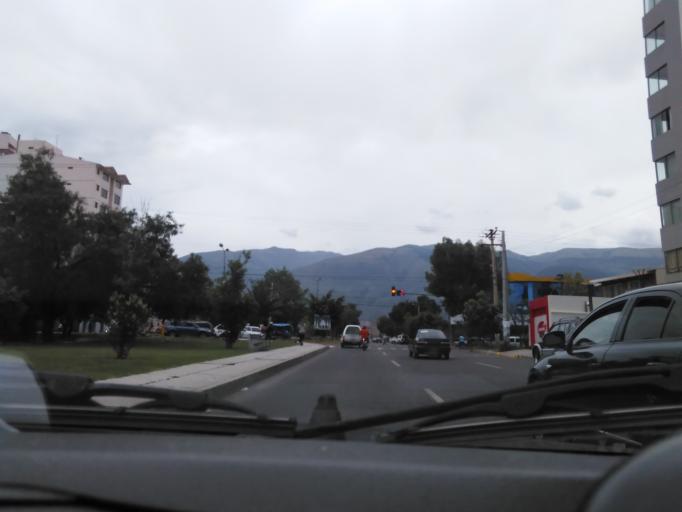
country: BO
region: Cochabamba
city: Cochabamba
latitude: -17.3719
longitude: -66.1801
